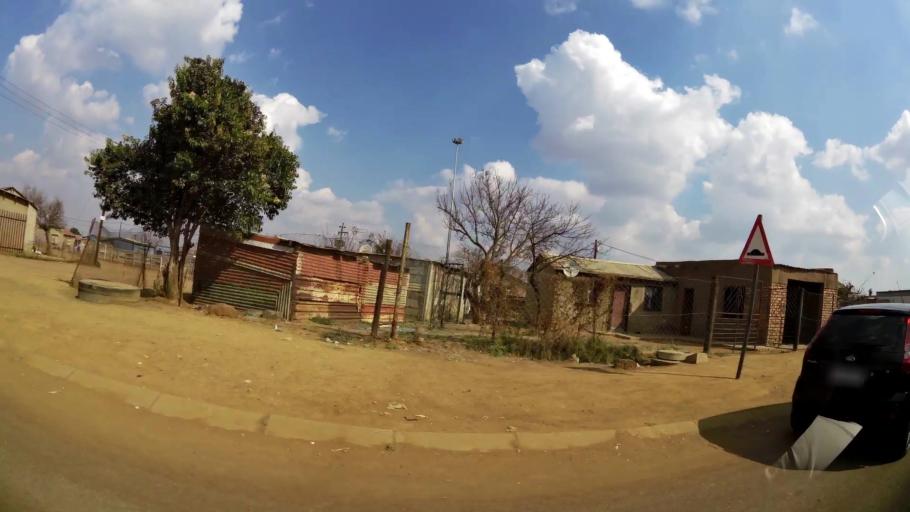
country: ZA
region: Gauteng
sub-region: Ekurhuleni Metropolitan Municipality
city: Springs
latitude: -26.1310
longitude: 28.4746
